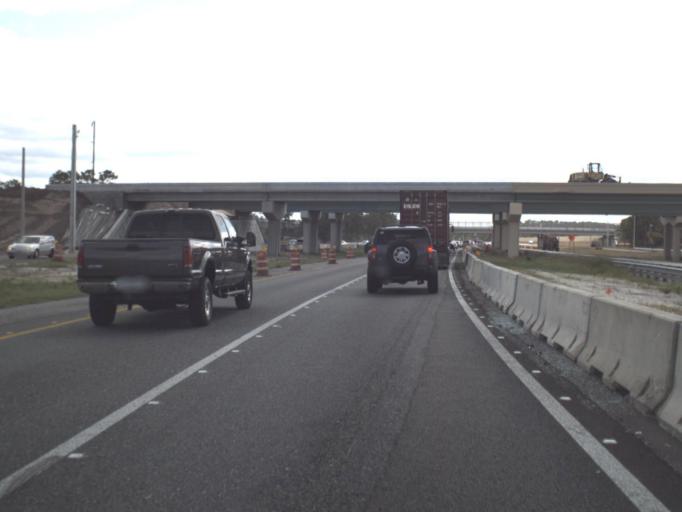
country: US
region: Florida
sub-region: Orange County
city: Southchase
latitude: 28.3695
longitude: -81.3897
